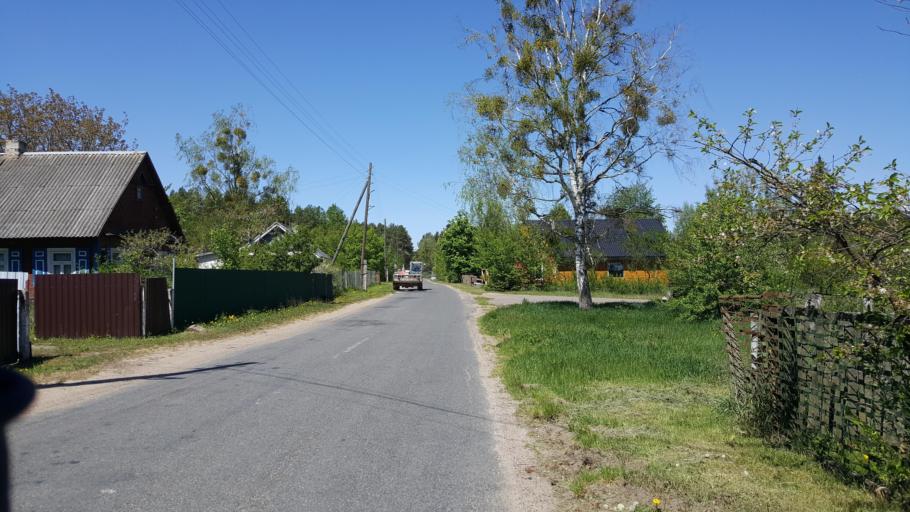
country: BY
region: Brest
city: Kamyanyuki
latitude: 52.5030
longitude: 23.7507
